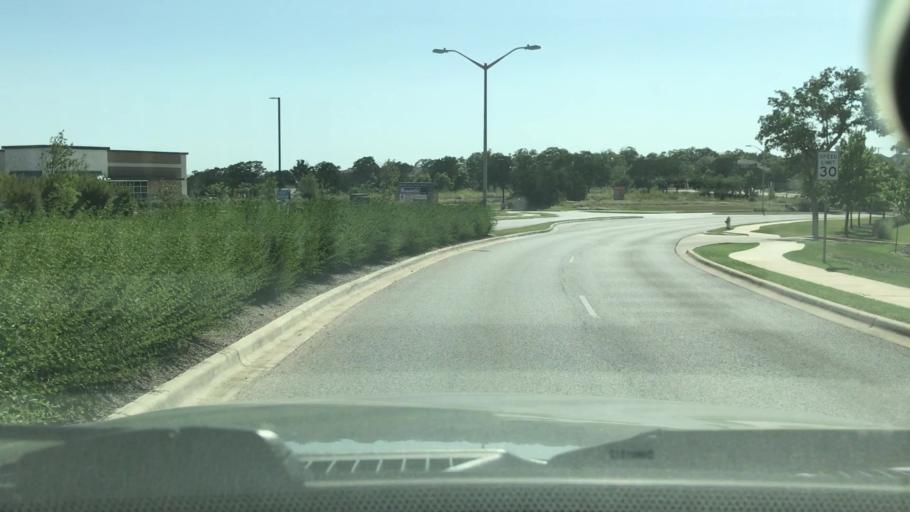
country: US
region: Texas
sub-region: Williamson County
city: Leander
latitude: 30.5452
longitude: -97.8652
